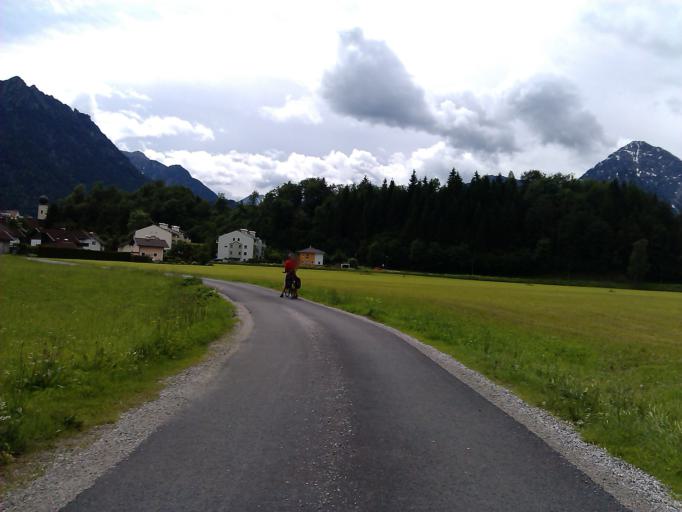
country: AT
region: Tyrol
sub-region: Politischer Bezirk Reutte
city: Lechaschau
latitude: 47.4918
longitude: 10.7115
